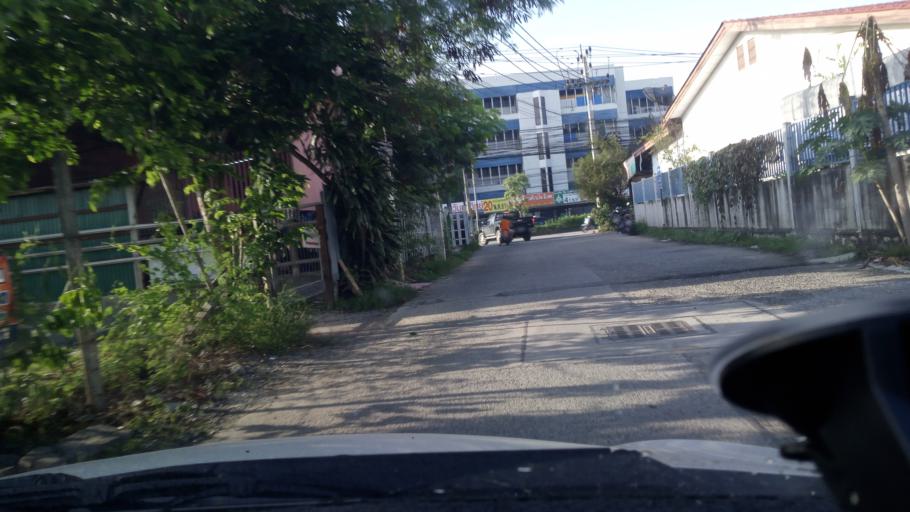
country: TH
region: Chon Buri
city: Phan Thong
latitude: 13.4145
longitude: 101.0614
